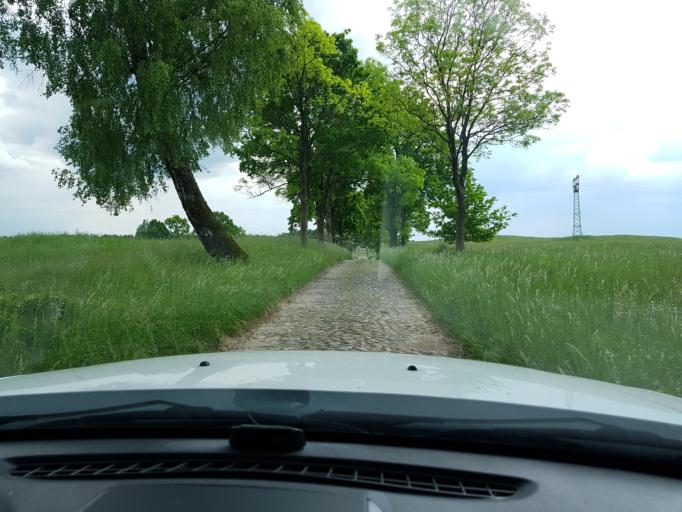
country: PL
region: West Pomeranian Voivodeship
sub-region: Powiat drawski
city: Drawsko Pomorskie
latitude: 53.5525
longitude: 15.7243
